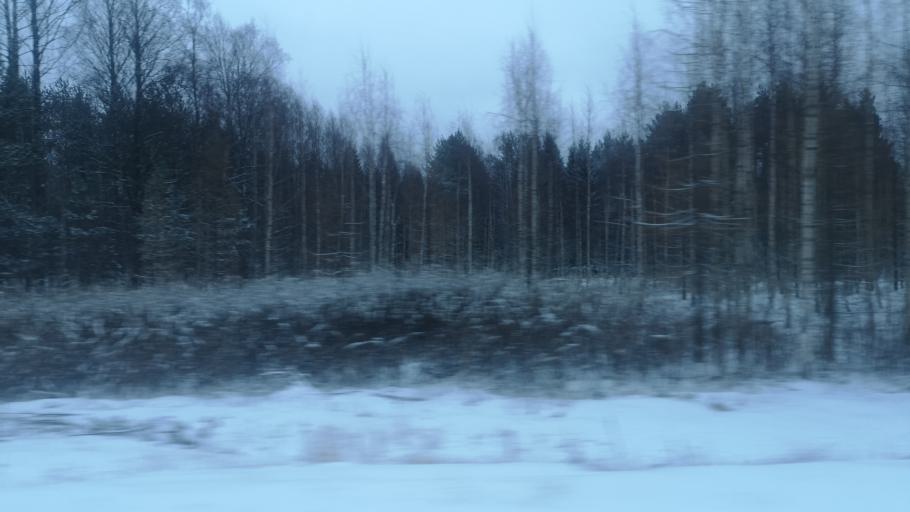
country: FI
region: Southern Savonia
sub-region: Savonlinna
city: Enonkoski
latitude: 62.0451
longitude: 28.7043
